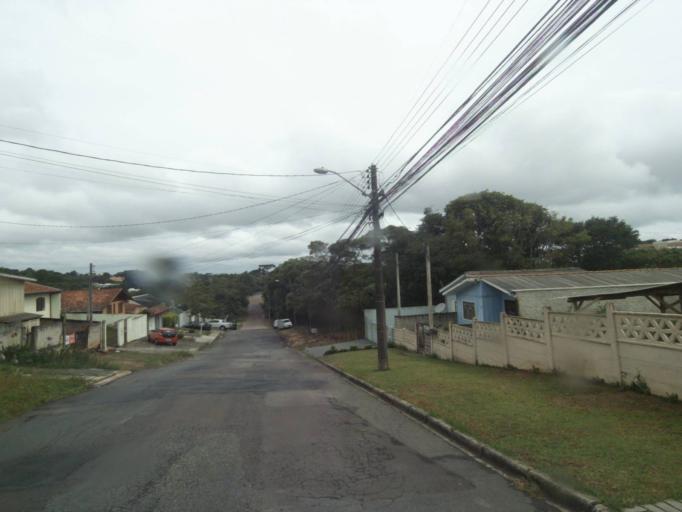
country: BR
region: Parana
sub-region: Curitiba
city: Curitiba
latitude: -25.4480
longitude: -49.3449
